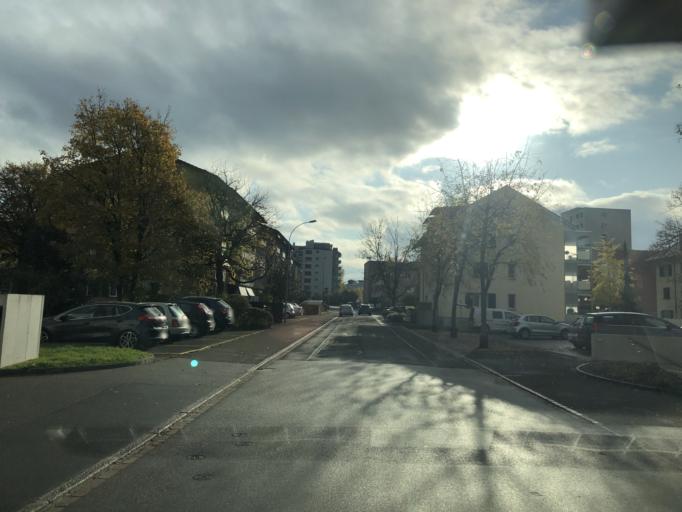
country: CH
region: Aargau
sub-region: Bezirk Baden
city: Neuenhof
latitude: 47.4614
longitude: 8.3284
